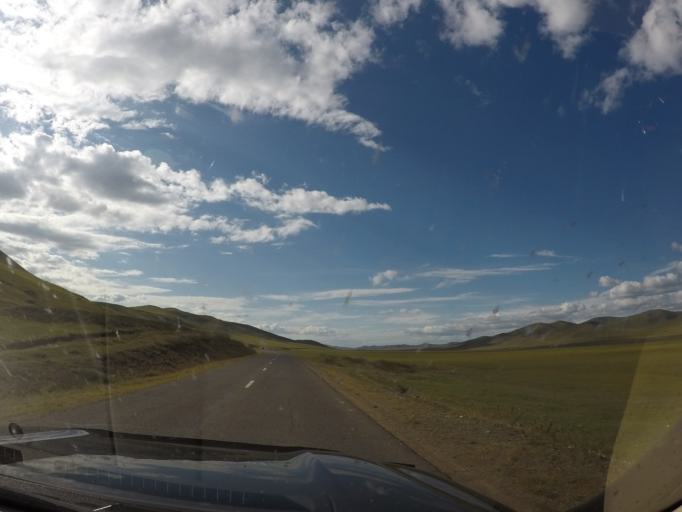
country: MN
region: Hentiy
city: Modot
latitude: 47.6808
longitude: 109.1090
